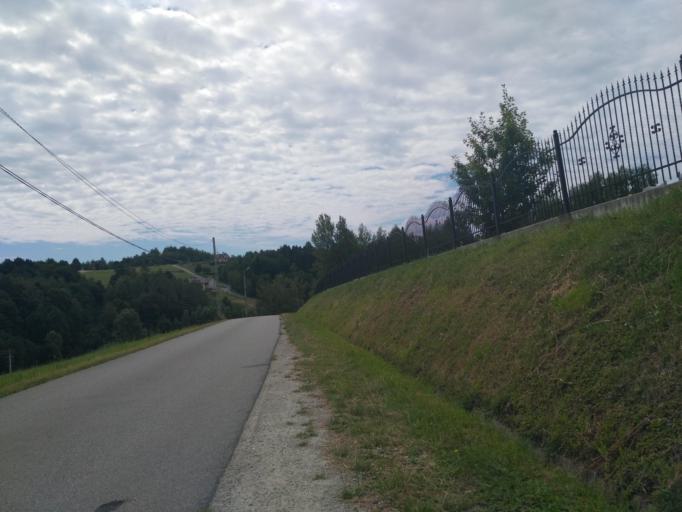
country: PL
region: Subcarpathian Voivodeship
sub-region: Powiat rzeszowski
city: Straszydle
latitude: 49.8957
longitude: 21.9807
